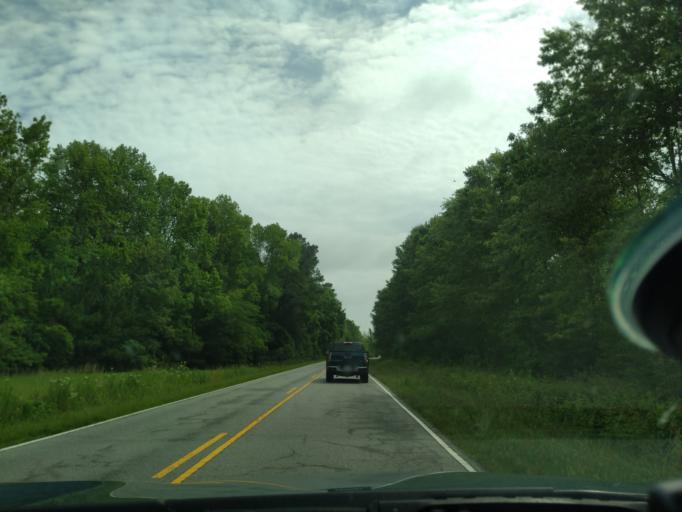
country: US
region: North Carolina
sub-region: Washington County
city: Plymouth
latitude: 35.8993
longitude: -76.6924
